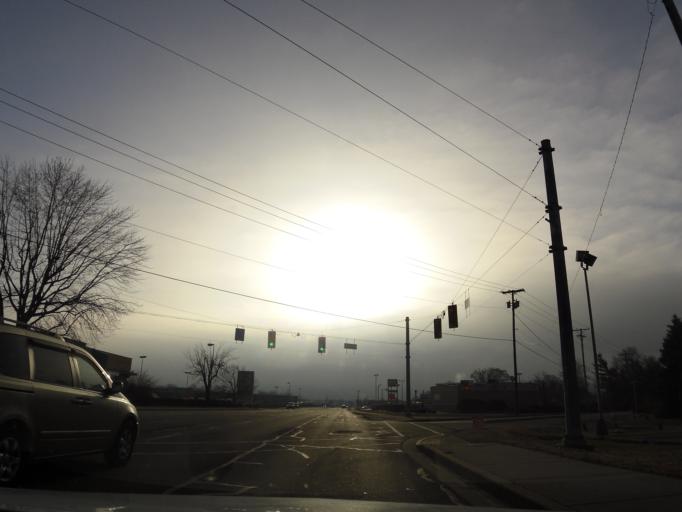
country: US
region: Indiana
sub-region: Bartholomew County
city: Columbus
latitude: 39.2208
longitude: -85.8884
